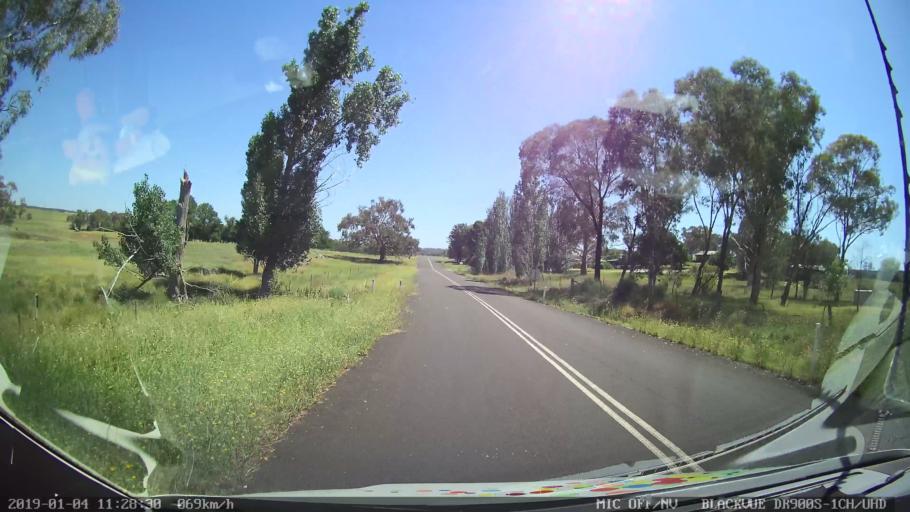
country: AU
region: New South Wales
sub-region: Cabonne
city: Molong
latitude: -33.0992
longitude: 148.7722
